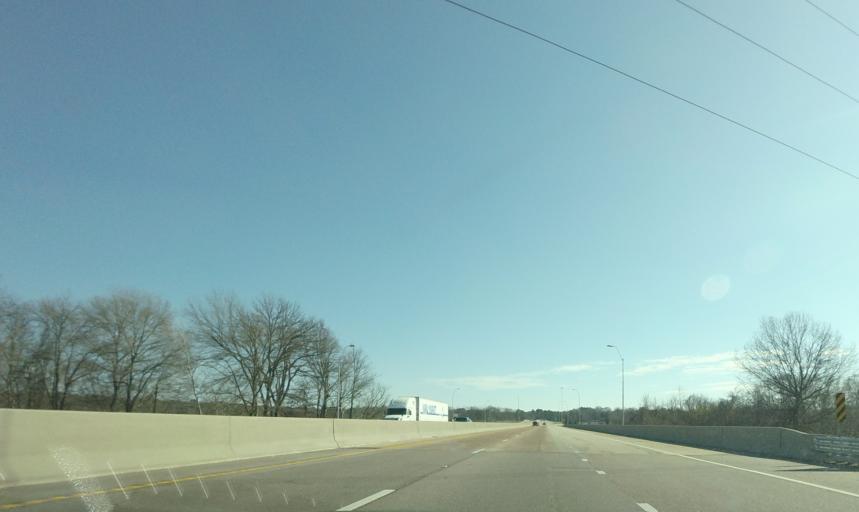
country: US
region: Mississippi
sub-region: Union County
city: New Albany
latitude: 34.4851
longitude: -89.0211
